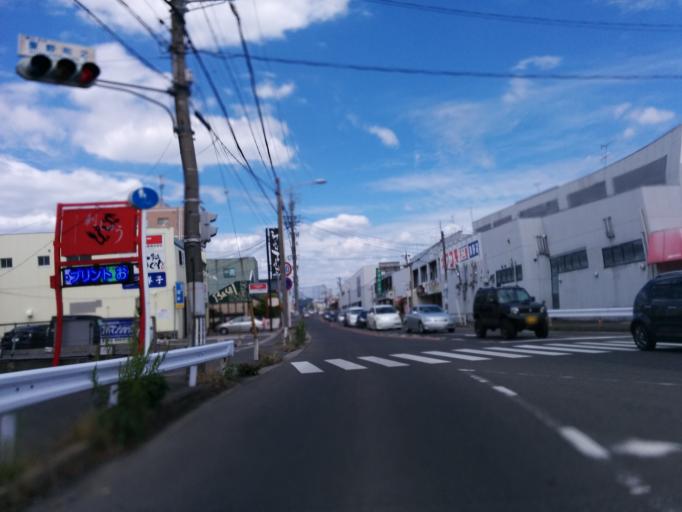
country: JP
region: Aichi
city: Kasugai
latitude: 35.2647
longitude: 136.9825
